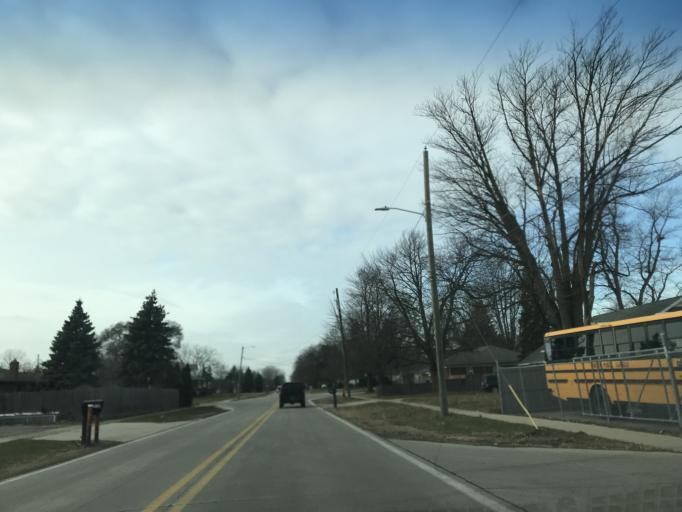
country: US
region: Michigan
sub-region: Macomb County
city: Fraser
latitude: 42.5315
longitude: -82.9529
